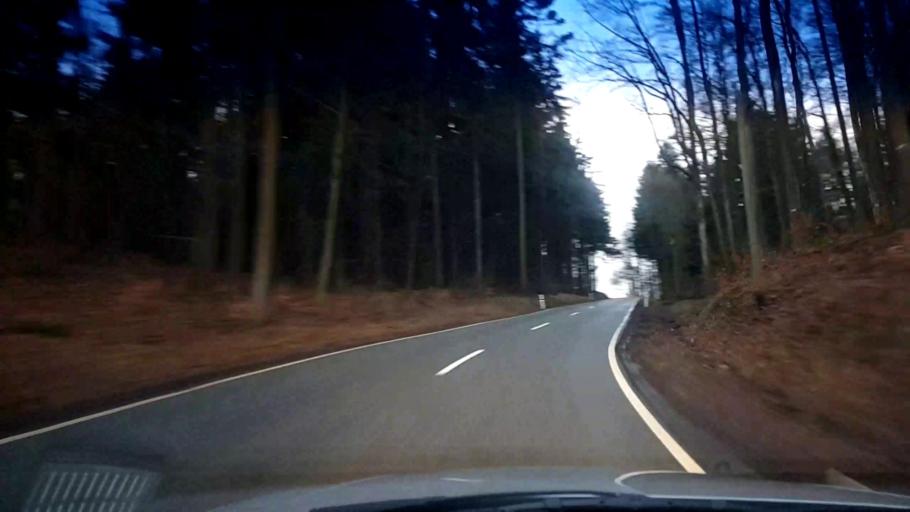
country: DE
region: Bavaria
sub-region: Upper Franconia
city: Wattendorf
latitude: 50.0481
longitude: 11.0615
